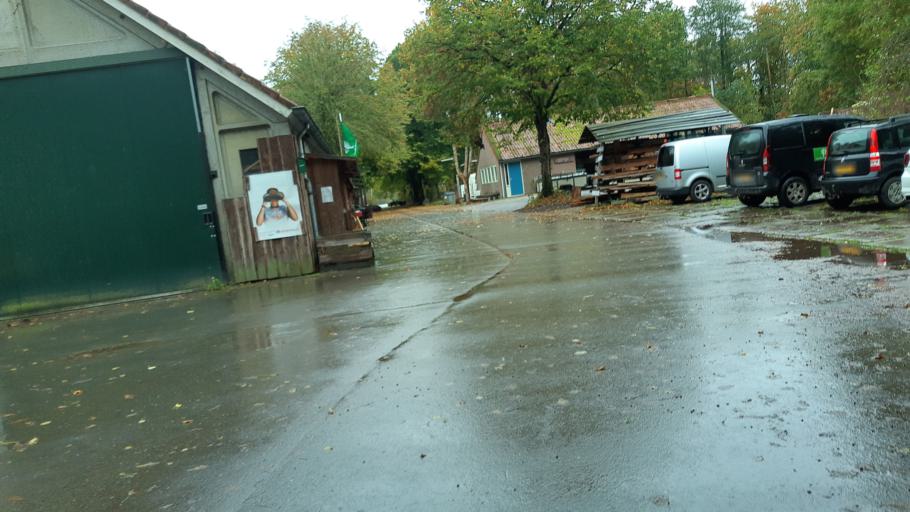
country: NL
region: Friesland
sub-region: Gemeente Lemsterland
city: Echtenerbrug
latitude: 52.7886
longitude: 5.7990
